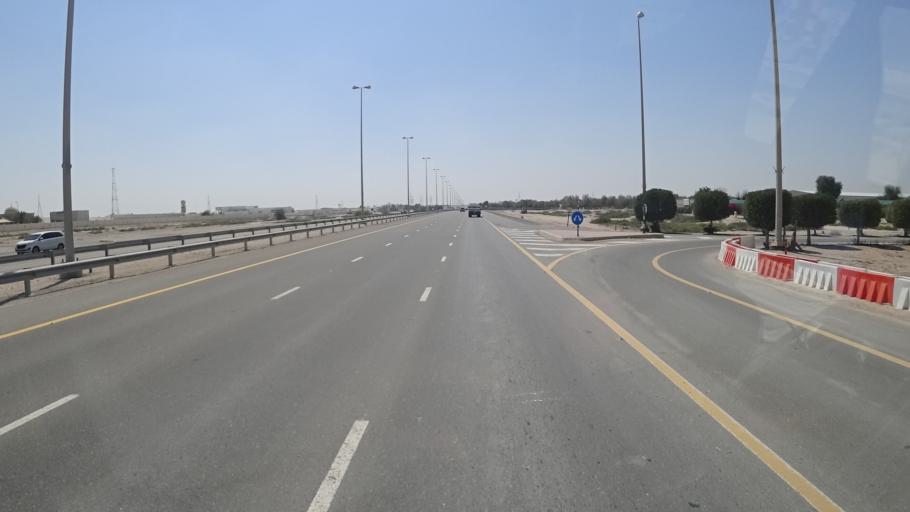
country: AE
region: Abu Dhabi
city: Abu Dhabi
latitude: 24.3097
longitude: 54.6738
